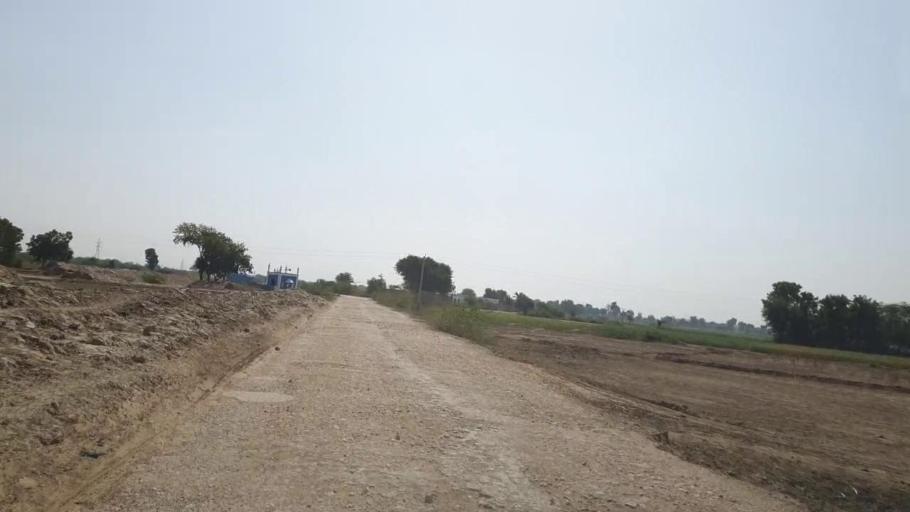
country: PK
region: Sindh
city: Naukot
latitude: 25.0023
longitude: 69.4656
